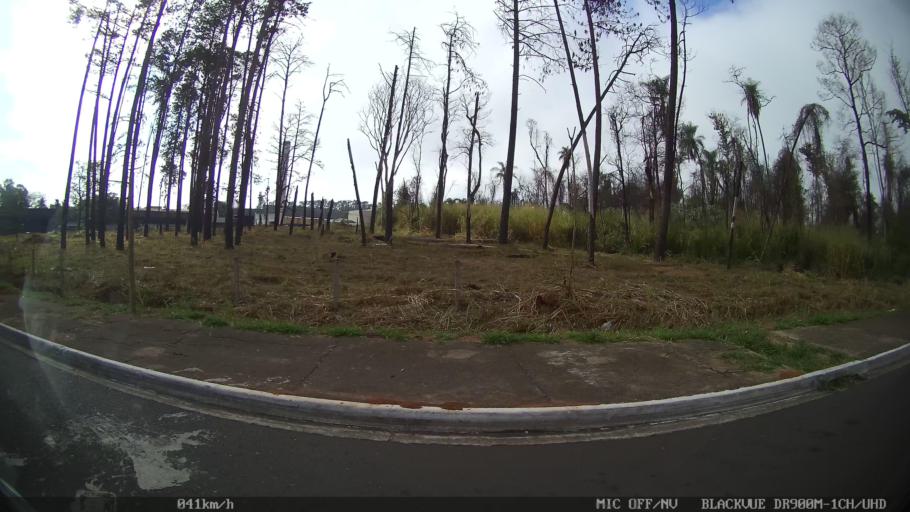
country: BR
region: Sao Paulo
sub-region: Sao Jose Do Rio Preto
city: Sao Jose do Rio Preto
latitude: -20.8167
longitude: -49.4341
